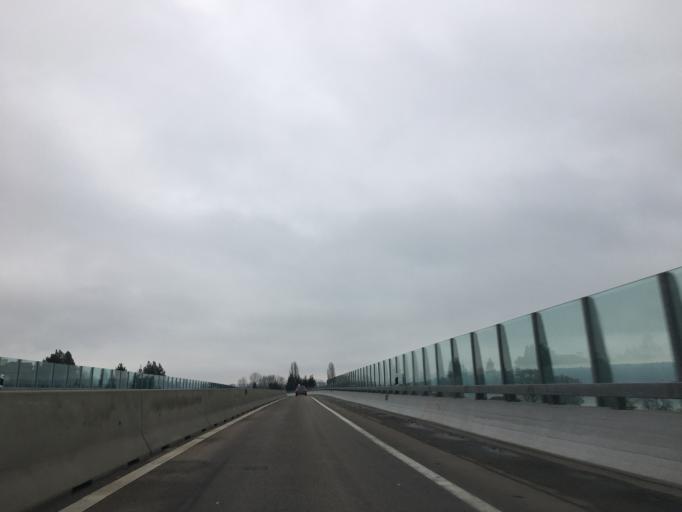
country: CH
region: Neuchatel
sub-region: Neuchatel District
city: Le Landeron
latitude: 47.0599
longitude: 7.0784
